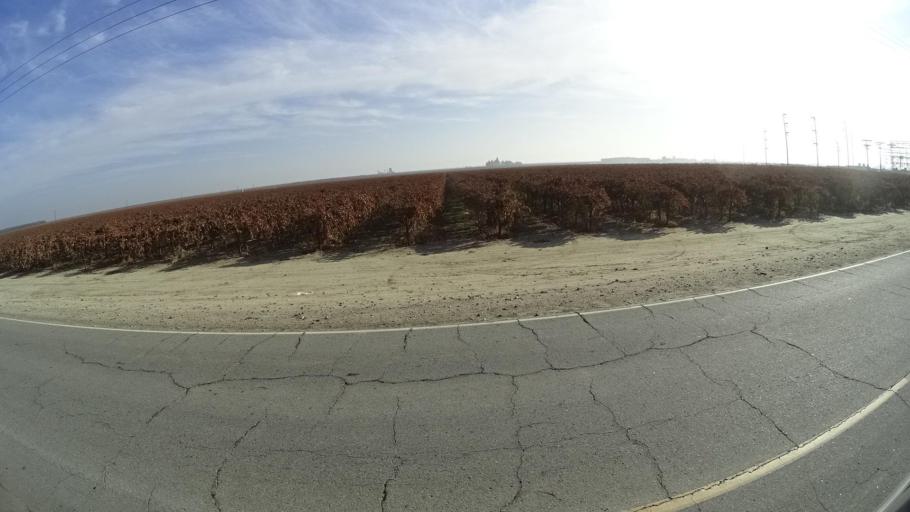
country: US
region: California
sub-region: Kern County
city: McFarland
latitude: 35.6067
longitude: -119.2044
